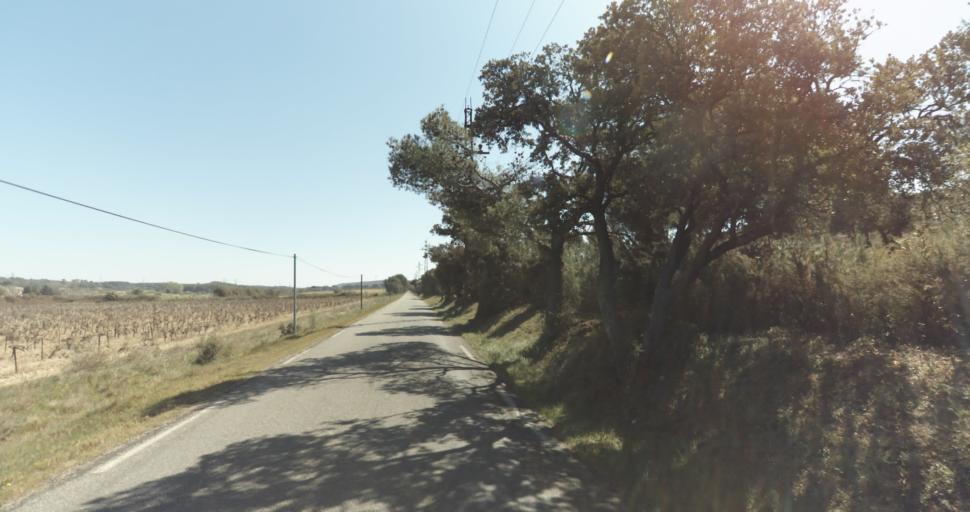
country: FR
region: Provence-Alpes-Cote d'Azur
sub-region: Departement des Bouches-du-Rhone
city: La Fare-les-Oliviers
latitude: 43.6019
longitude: 5.1938
